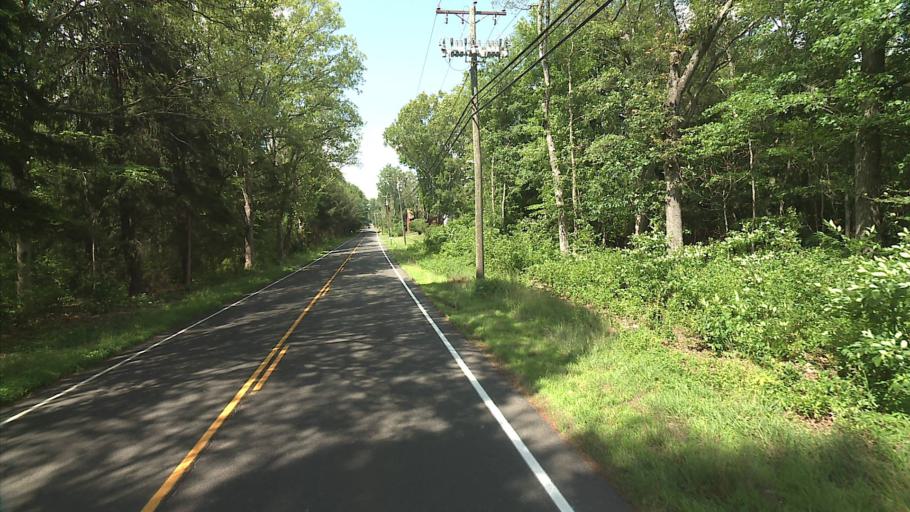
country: US
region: Connecticut
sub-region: Middlesex County
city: Higganum
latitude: 41.3925
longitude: -72.5624
